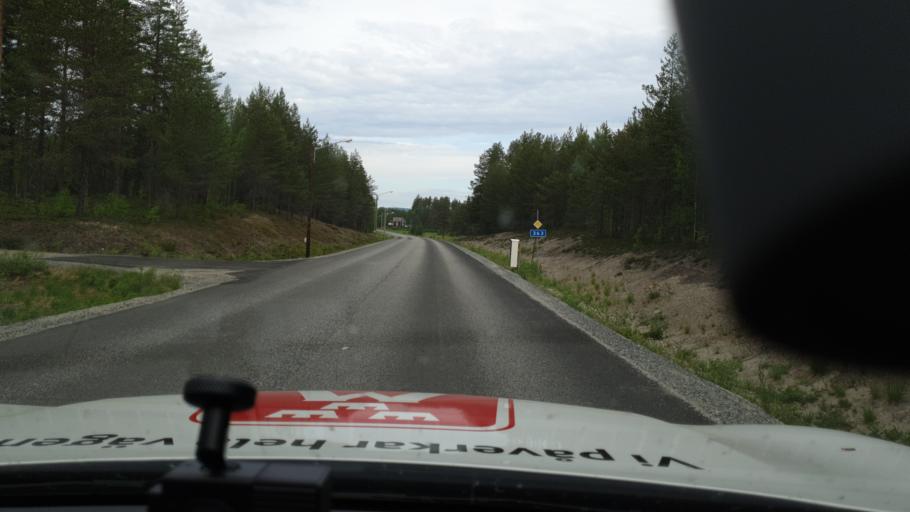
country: SE
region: Vaesterbotten
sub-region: Mala Kommun
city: Mala
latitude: 64.9080
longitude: 18.6766
